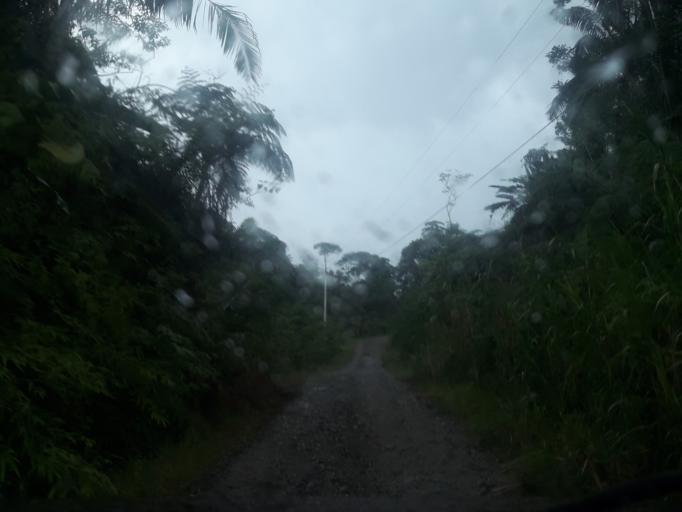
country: EC
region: Napo
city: Tena
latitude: -1.0992
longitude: -77.6942
